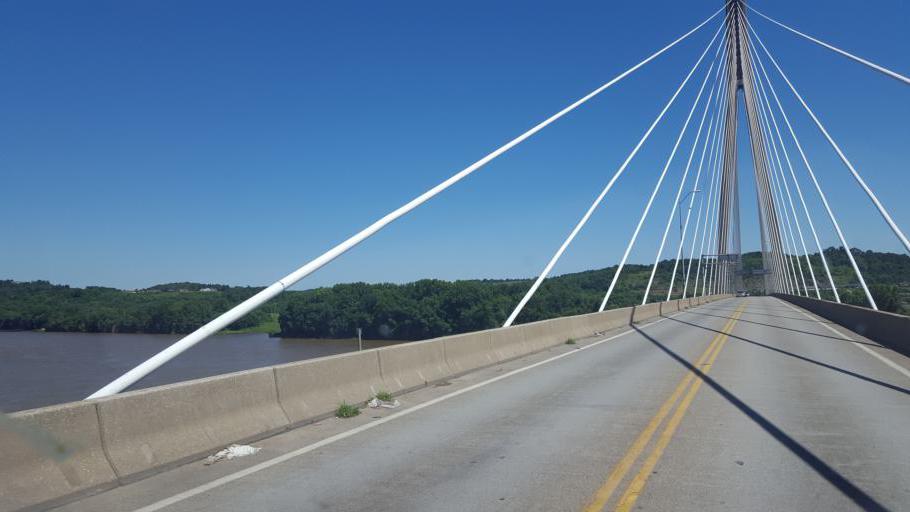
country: US
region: West Virginia
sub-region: Cabell County
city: Huntington
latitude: 38.4330
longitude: -82.3898
